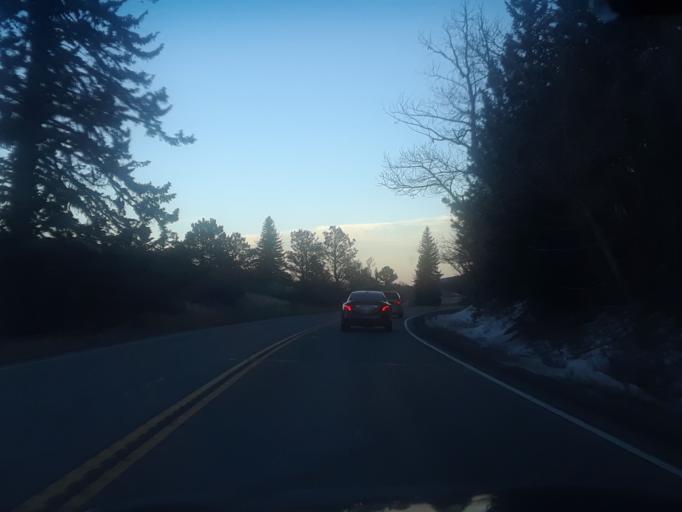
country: US
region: Colorado
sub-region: Clear Creek County
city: Georgetown
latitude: 39.4415
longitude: -105.6028
